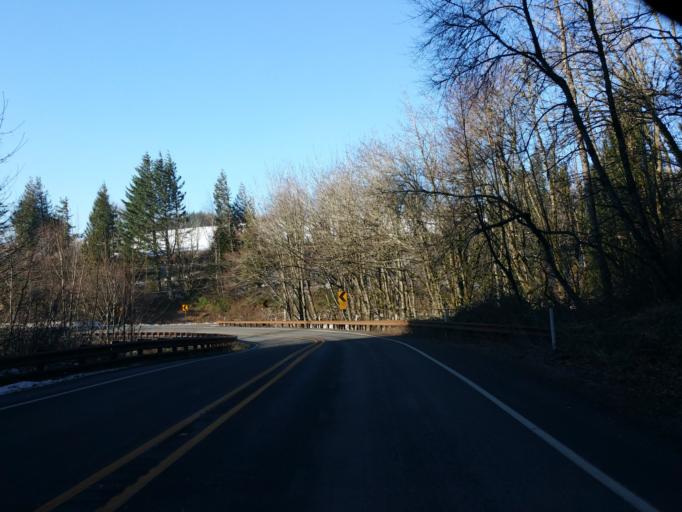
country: US
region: Washington
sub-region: Clark County
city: Washougal
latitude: 45.5660
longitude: -122.2171
